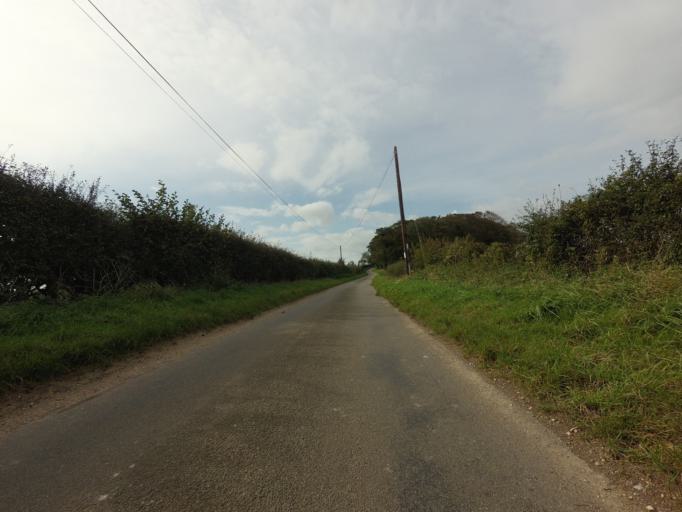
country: GB
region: England
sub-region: Norfolk
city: Wells-next-the-Sea
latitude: 52.9392
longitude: 0.6918
